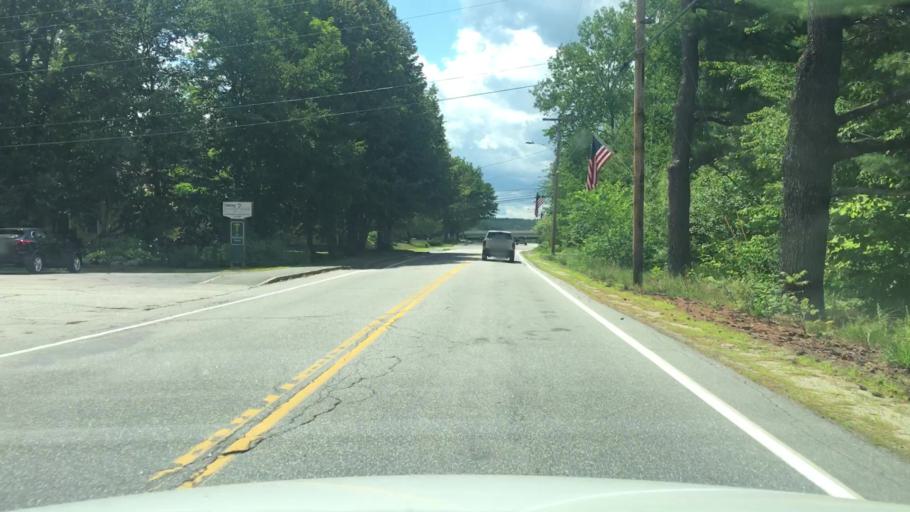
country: US
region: Maine
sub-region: Oxford County
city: Bethel
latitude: 44.4104
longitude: -70.7915
